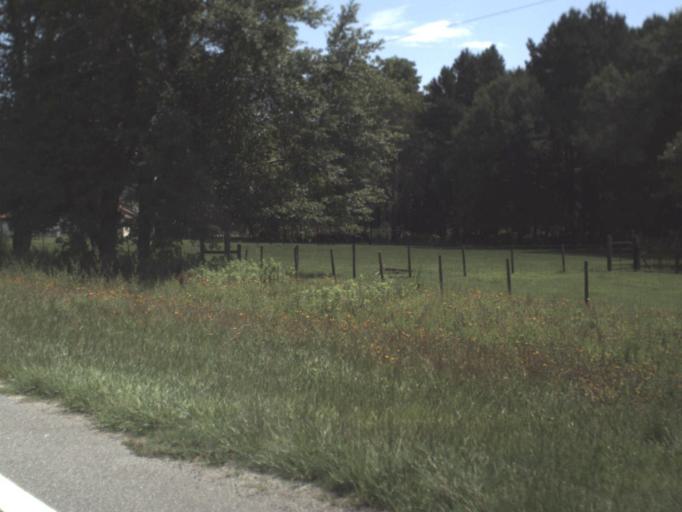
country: US
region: Florida
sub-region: Hamilton County
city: Jasper
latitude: 30.4863
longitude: -82.9301
